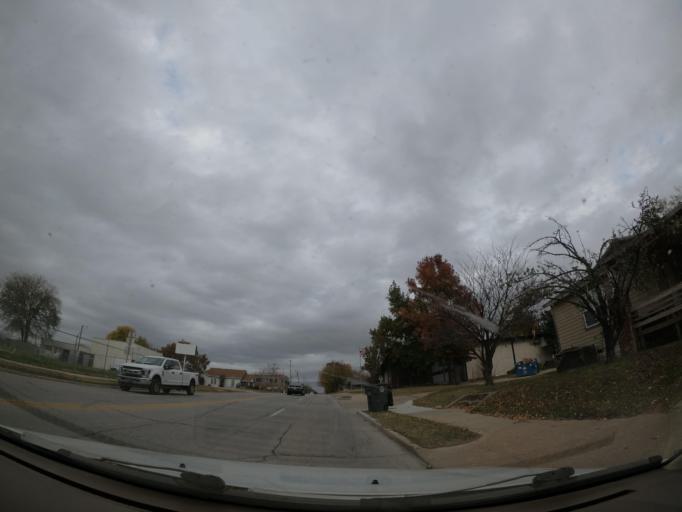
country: US
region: Oklahoma
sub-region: Tulsa County
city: Tulsa
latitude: 36.1617
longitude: -95.9670
